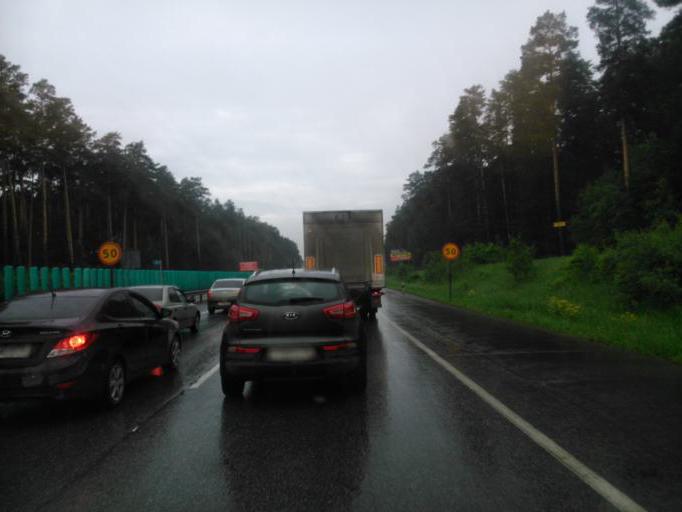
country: RU
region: Sverdlovsk
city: Istok
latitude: 56.7828
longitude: 60.8419
